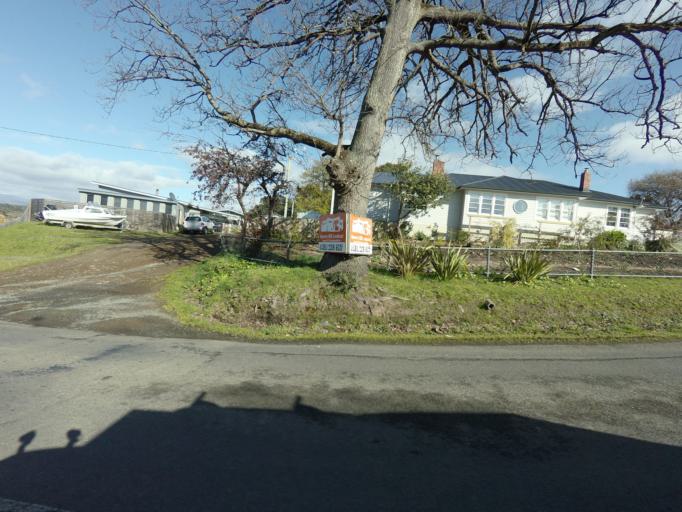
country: AU
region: Tasmania
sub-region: Huon Valley
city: Cygnet
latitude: -43.3143
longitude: 147.0151
